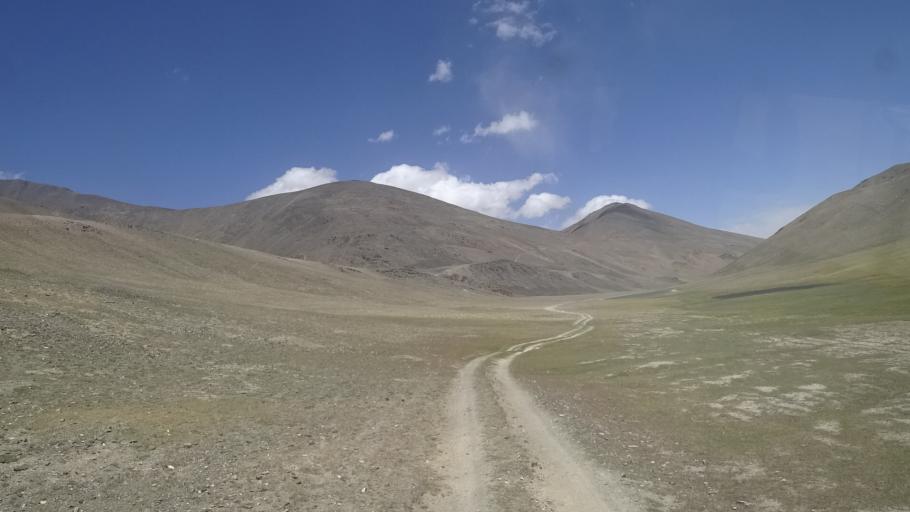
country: TJ
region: Gorno-Badakhshan
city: Murghob
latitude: 37.5168
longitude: 74.0573
